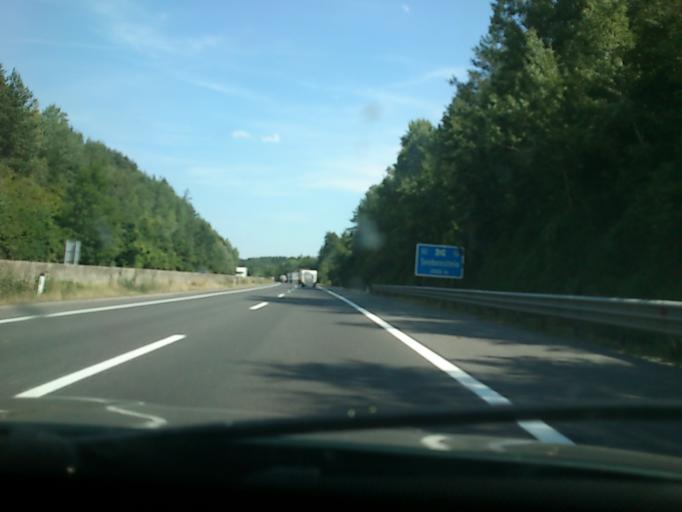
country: AT
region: Lower Austria
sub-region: Politischer Bezirk Neunkirchen
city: Seebenstein
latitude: 47.6897
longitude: 16.1281
